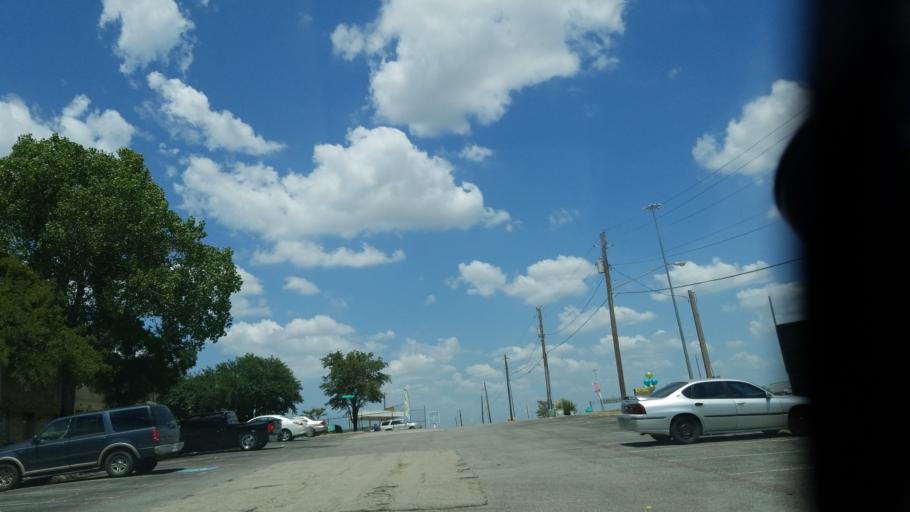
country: US
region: Texas
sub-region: Dallas County
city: Cockrell Hill
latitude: 32.7337
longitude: -96.9207
